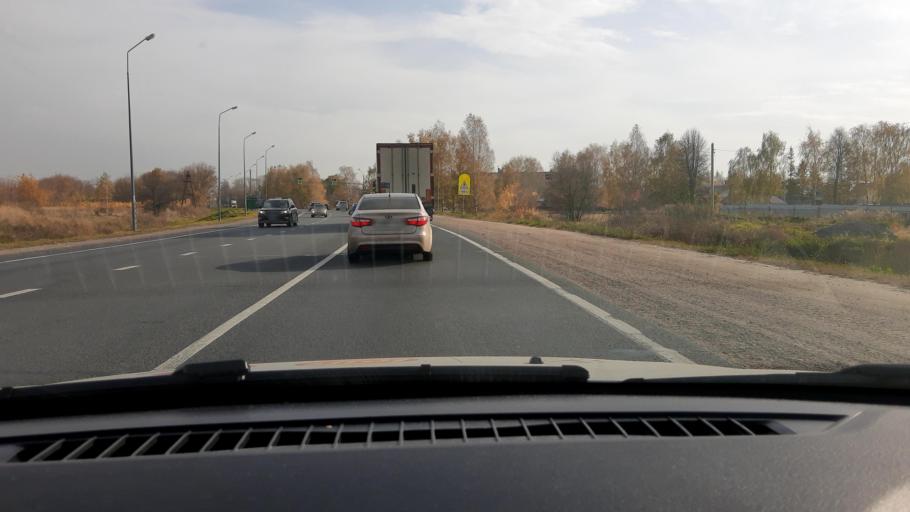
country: RU
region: Nizjnij Novgorod
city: Pamyat' Parizhskoy Kommuny
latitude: 56.0430
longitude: 44.4415
